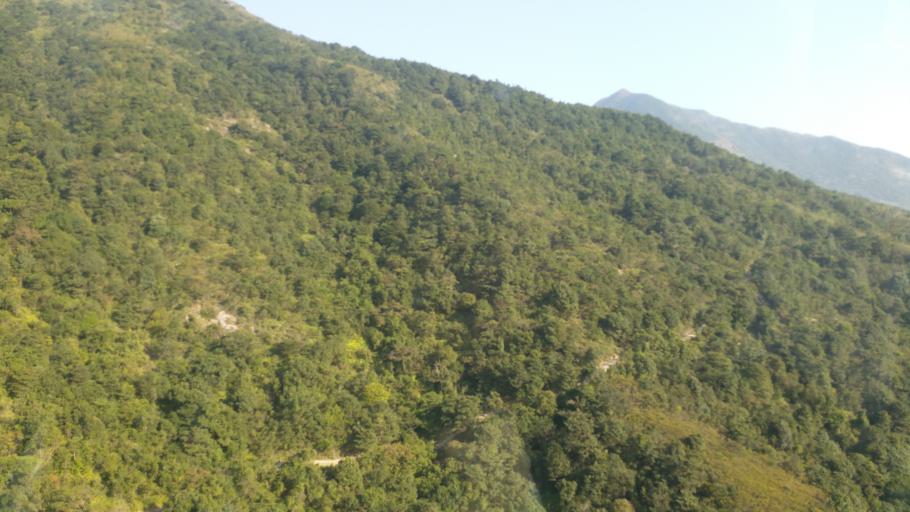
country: HK
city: Tai O
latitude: 22.2630
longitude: 113.9047
